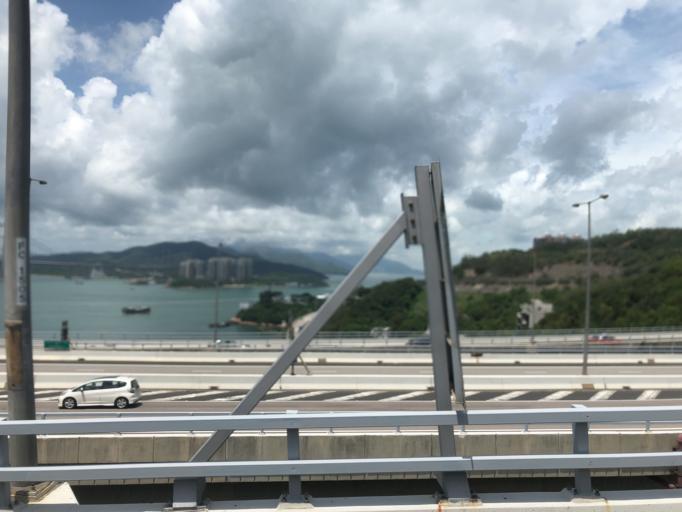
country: HK
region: Tsuen Wan
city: Tsuen Wan
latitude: 22.3698
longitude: 114.0768
